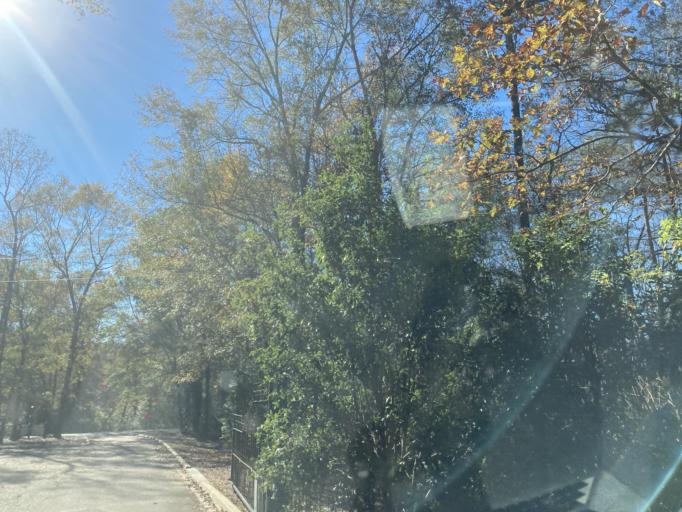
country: US
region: Mississippi
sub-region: Forrest County
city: Petal
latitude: 31.3287
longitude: -89.1680
